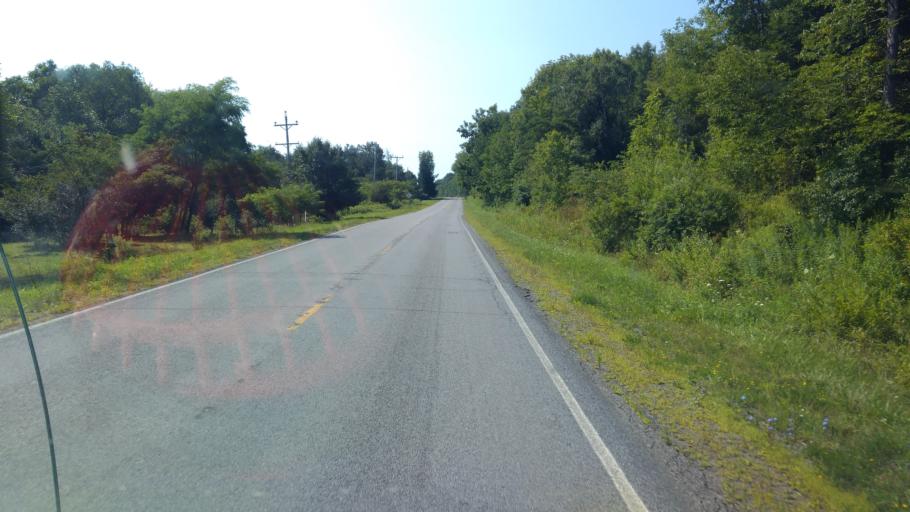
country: US
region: New York
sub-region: Allegany County
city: Friendship
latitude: 42.1479
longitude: -78.1497
